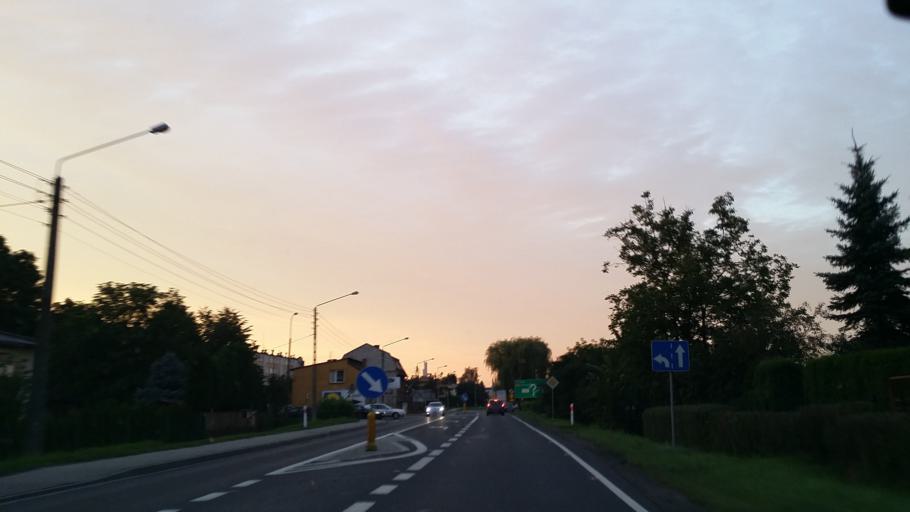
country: PL
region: Lesser Poland Voivodeship
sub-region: Powiat oswiecimski
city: Oswiecim
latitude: 50.0325
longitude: 19.2101
